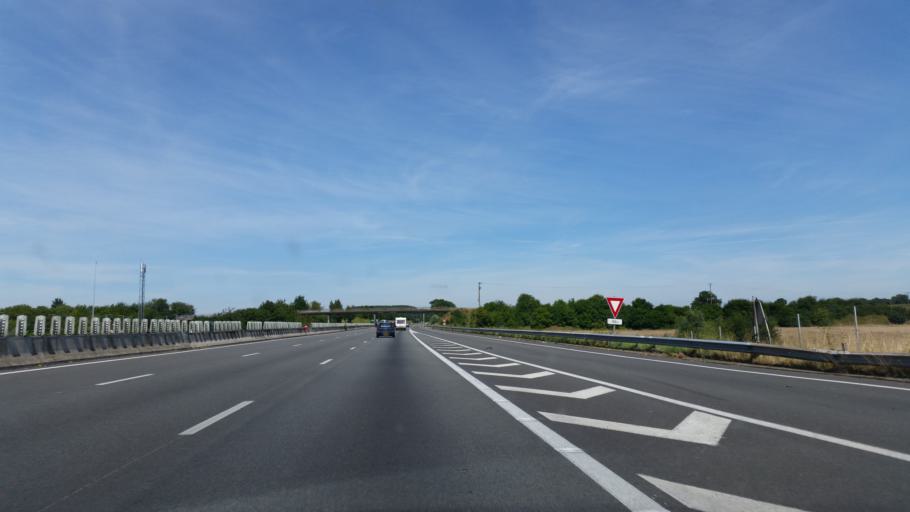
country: FR
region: Nord-Pas-de-Calais
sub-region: Departement du Pas-de-Calais
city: Bapaume
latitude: 50.0756
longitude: 2.8708
